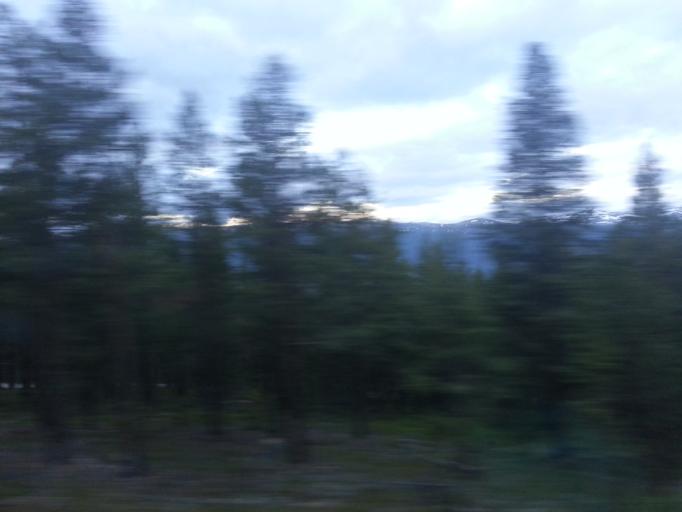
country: NO
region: Oppland
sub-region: Dovre
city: Dombas
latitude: 62.1100
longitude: 9.1125
